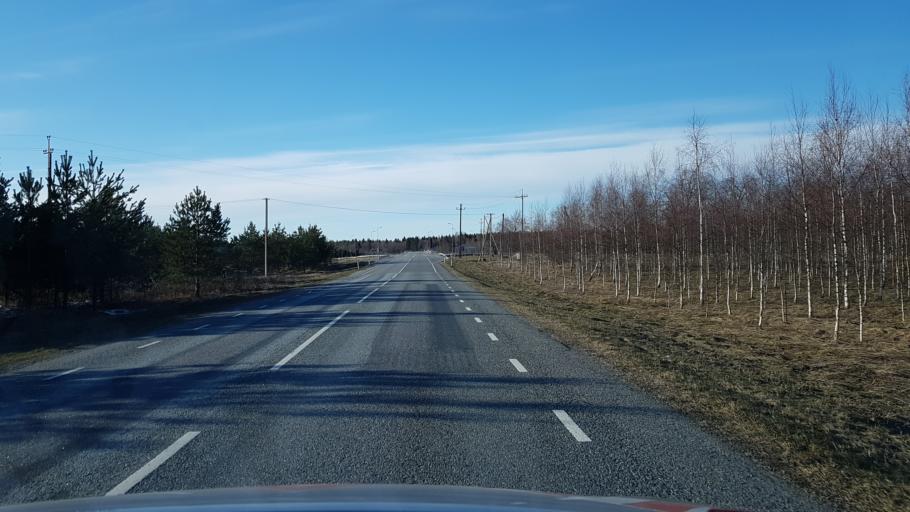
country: EE
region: Laeaene-Virumaa
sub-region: Tapa vald
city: Tapa
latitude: 59.4503
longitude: 25.9468
